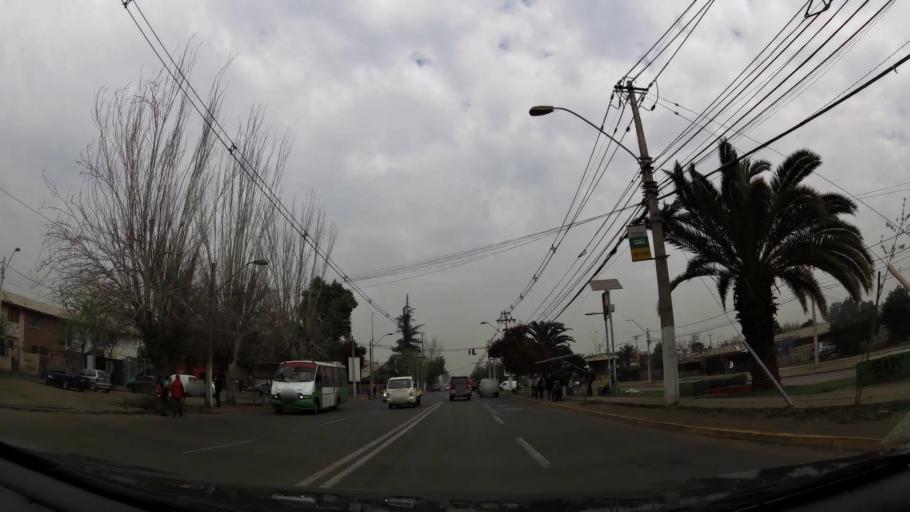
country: CL
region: Santiago Metropolitan
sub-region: Provincia de Chacabuco
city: Chicureo Abajo
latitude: -33.2092
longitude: -70.6797
